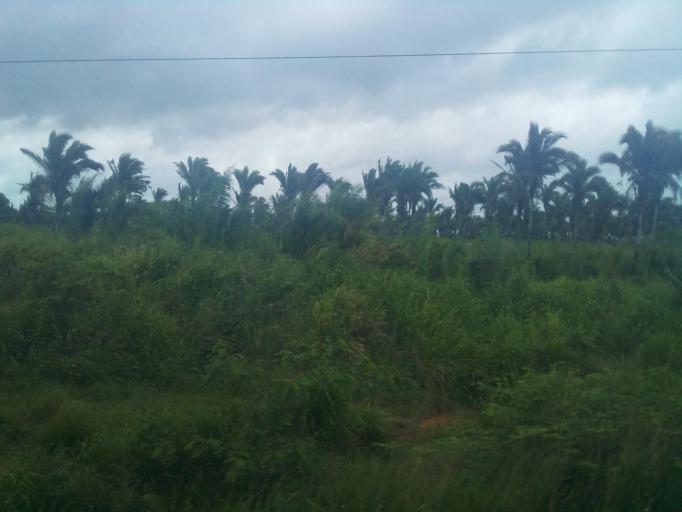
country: BR
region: Maranhao
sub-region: Arari
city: Arari
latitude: -3.5751
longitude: -44.7054
